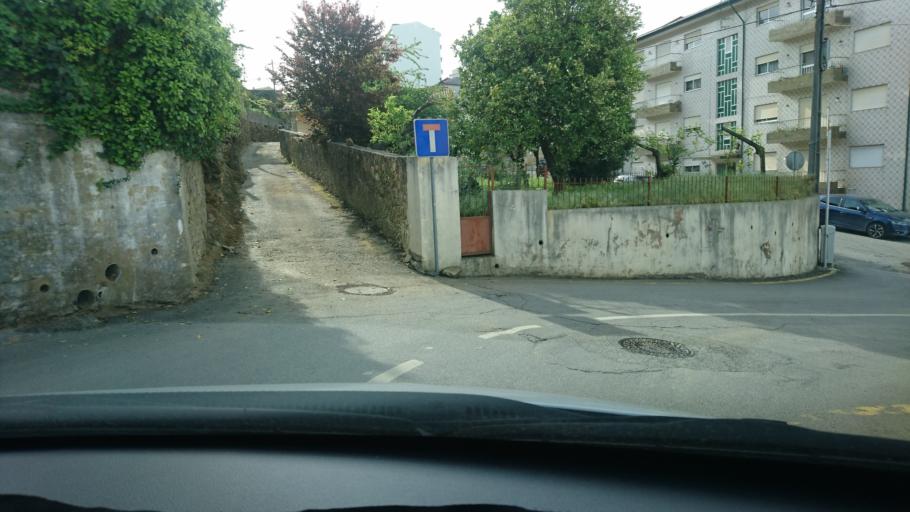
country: PT
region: Aveiro
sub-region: Oliveira de Azemeis
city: Oliveira de Azemeis
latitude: 40.8421
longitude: -8.4813
